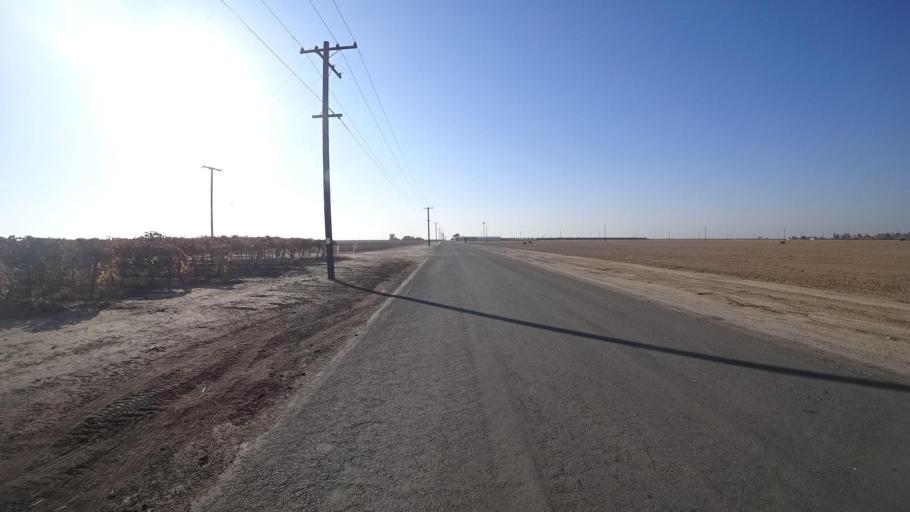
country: US
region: California
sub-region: Tulare County
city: Richgrove
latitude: 35.7817
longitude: -119.1607
